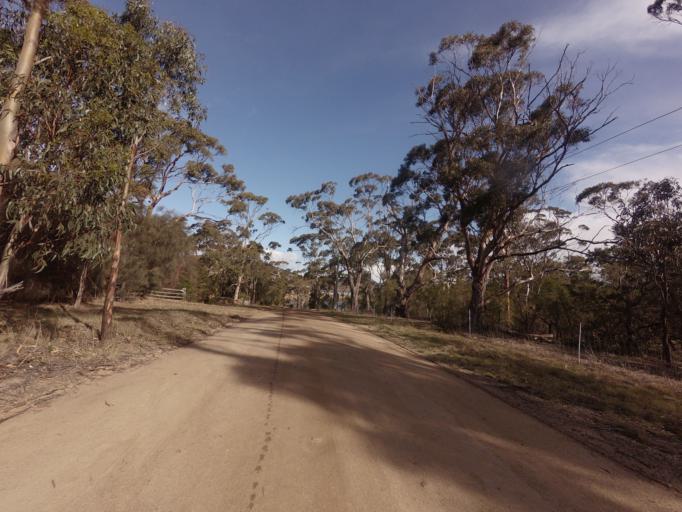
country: AU
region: Tasmania
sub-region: Sorell
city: Sorell
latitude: -42.3074
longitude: 147.9965
